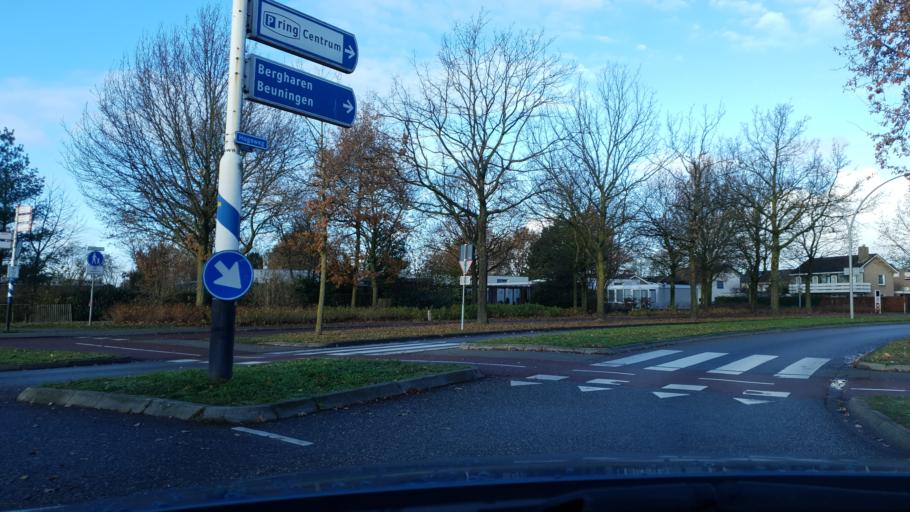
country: NL
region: Gelderland
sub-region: Gemeente Wijchen
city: Wijchen
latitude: 51.8053
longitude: 5.7203
